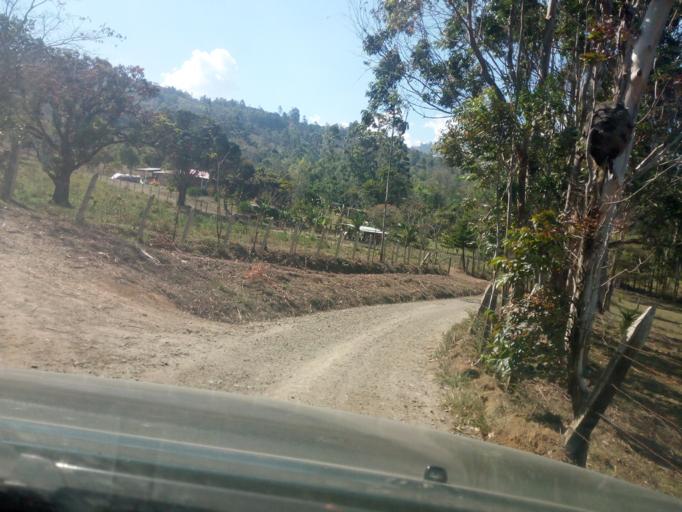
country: CO
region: Boyaca
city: Guateque
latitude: 4.9941
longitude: -73.4642
